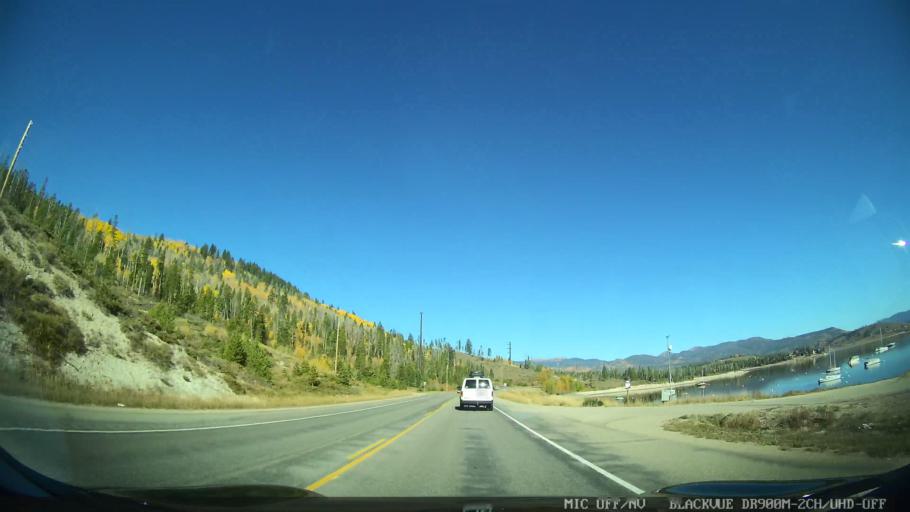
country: US
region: Colorado
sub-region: Grand County
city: Granby
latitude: 40.1609
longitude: -105.8950
